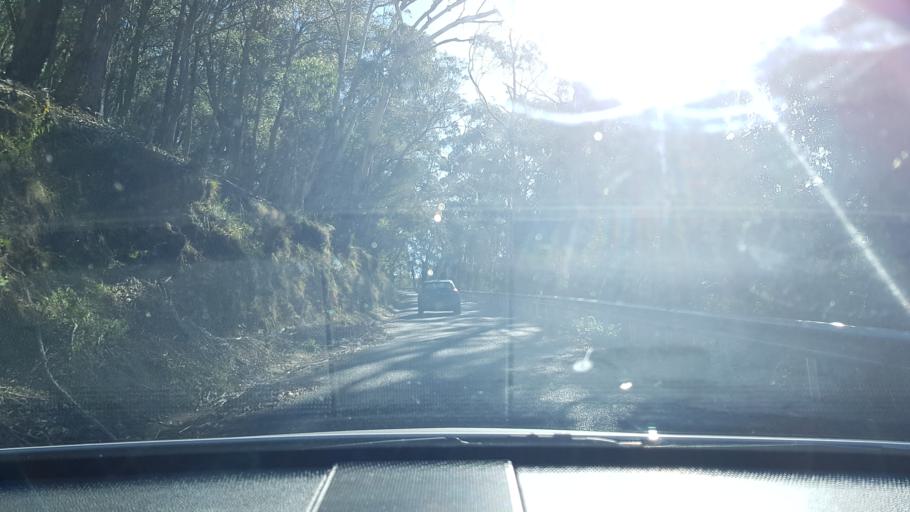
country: AU
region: New South Wales
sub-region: Oberon
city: Oberon
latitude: -33.8163
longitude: 150.0144
